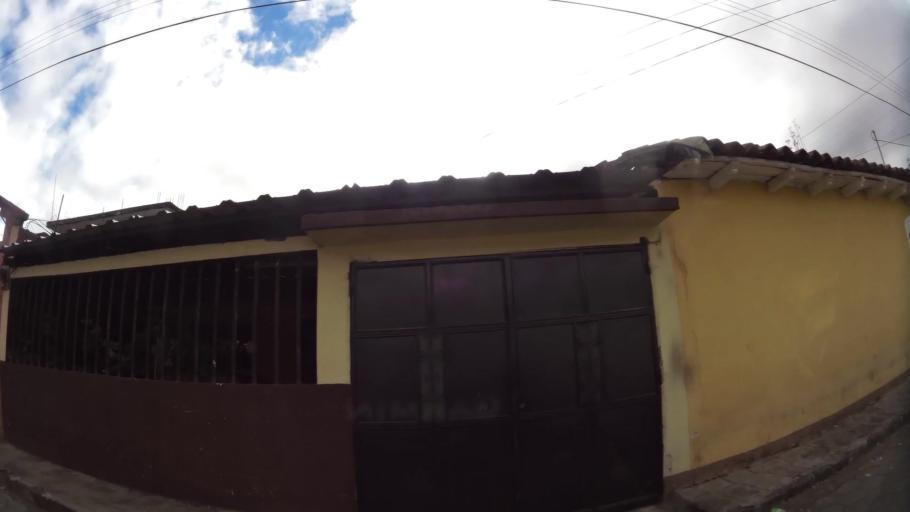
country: GT
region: Quetzaltenango
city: Salcaja
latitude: 14.8785
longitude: -91.4528
